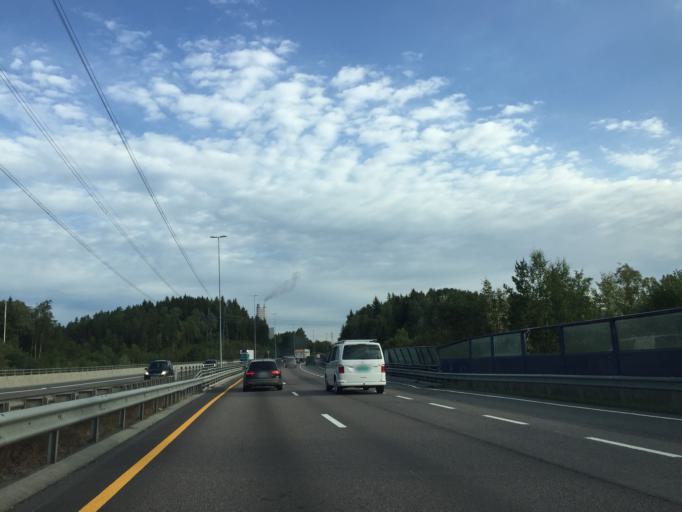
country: NO
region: Akershus
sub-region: Oppegard
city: Kolbotn
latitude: 59.8334
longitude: 10.8403
